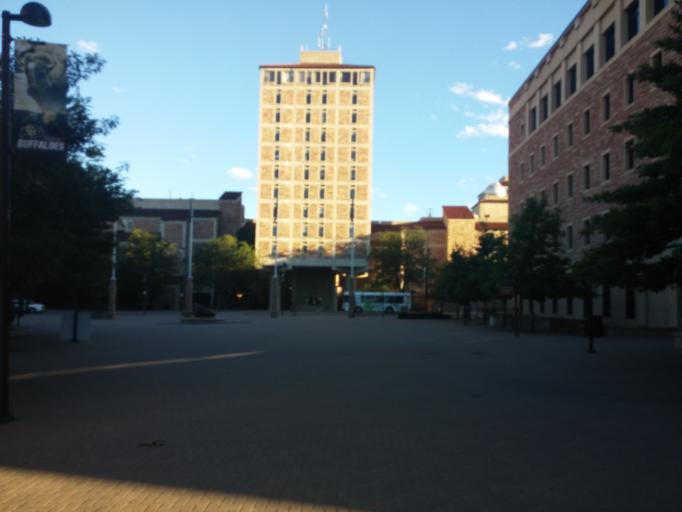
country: US
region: Colorado
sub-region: Boulder County
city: Boulder
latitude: 40.0089
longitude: -105.2679
